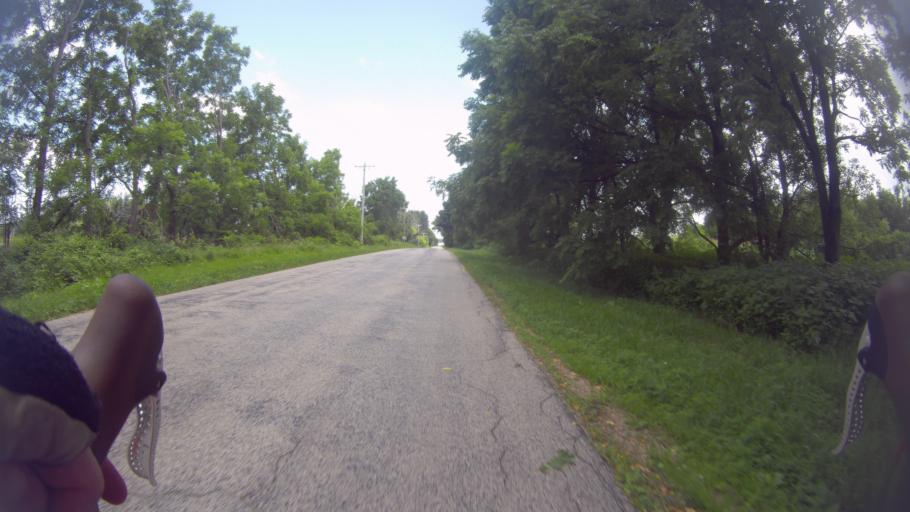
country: US
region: Wisconsin
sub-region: Columbia County
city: Lodi
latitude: 43.2307
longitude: -89.5966
